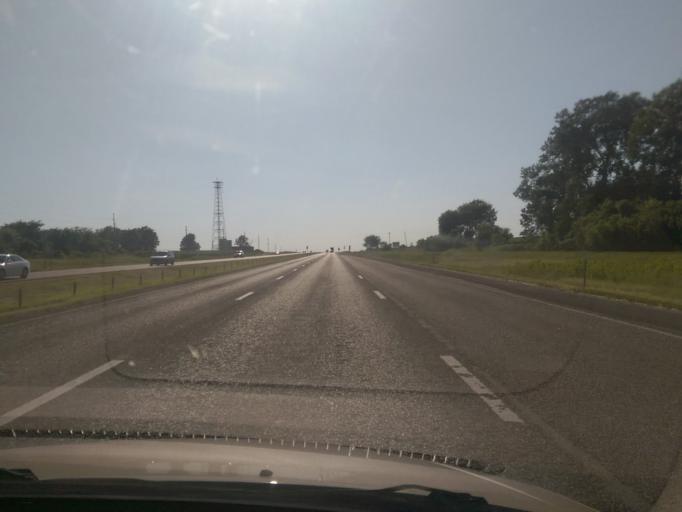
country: US
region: Missouri
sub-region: Lafayette County
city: Higginsville
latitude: 38.9924
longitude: -93.6759
